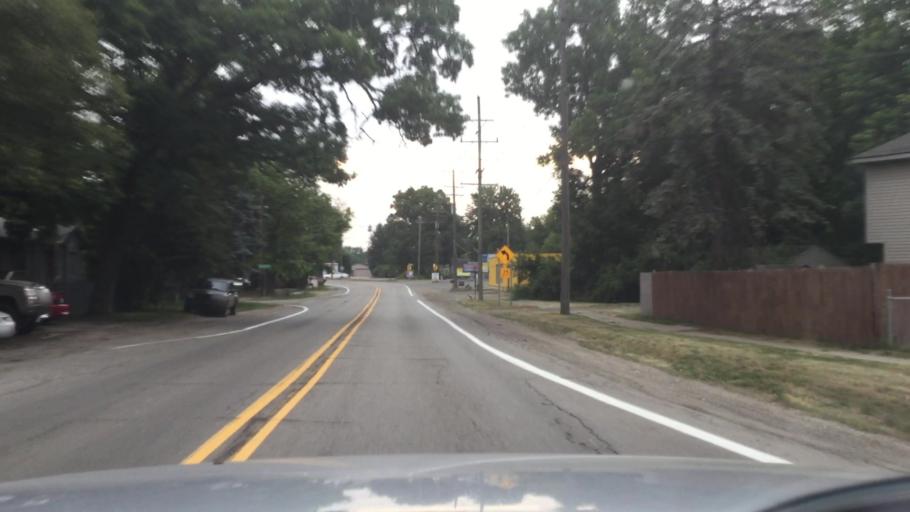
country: US
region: Michigan
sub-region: Oakland County
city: Waterford
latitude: 42.6812
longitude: -83.4270
